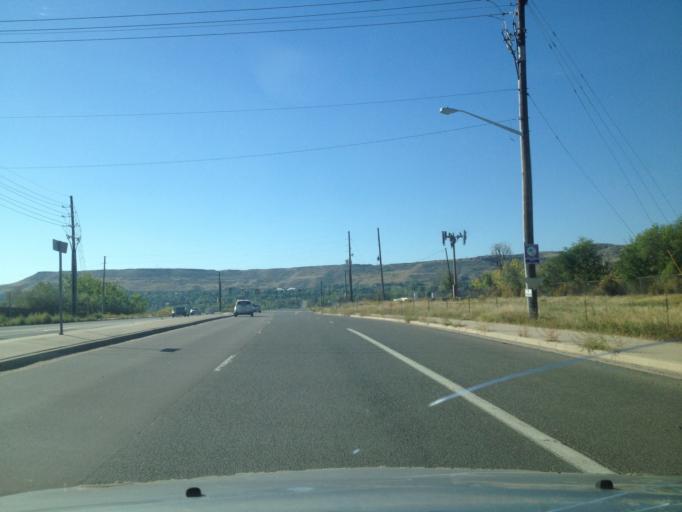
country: US
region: Colorado
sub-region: Jefferson County
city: Applewood
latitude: 39.7755
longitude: -105.1749
